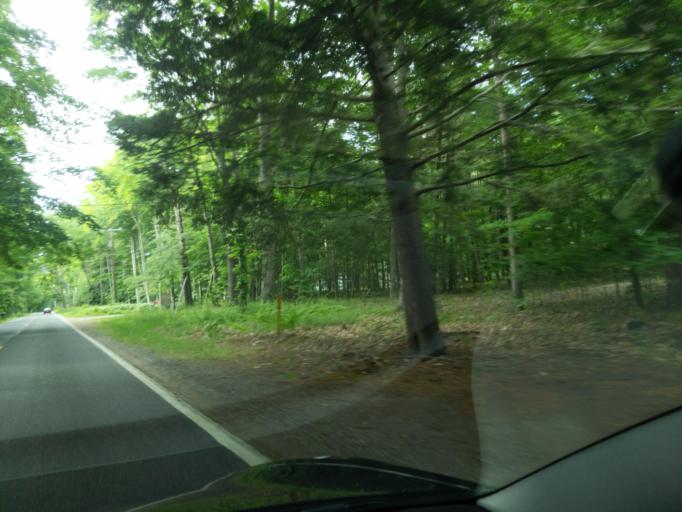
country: US
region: Michigan
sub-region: Muskegon County
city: Whitehall
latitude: 43.3074
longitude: -86.3866
